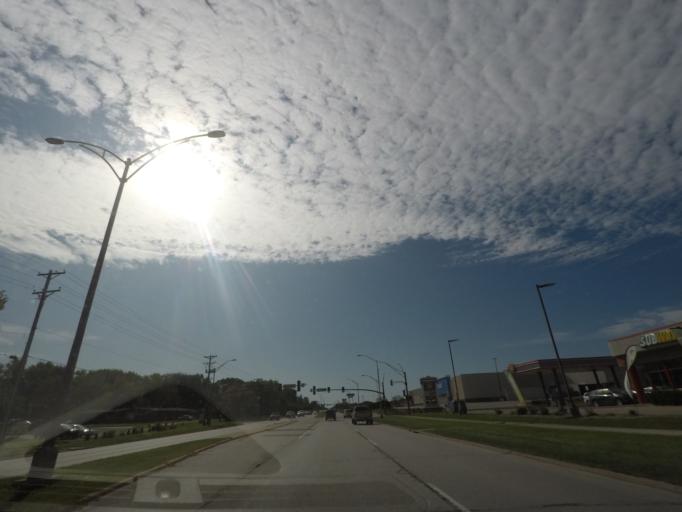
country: US
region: Iowa
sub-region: Story County
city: Ames
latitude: 42.0525
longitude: -93.6202
